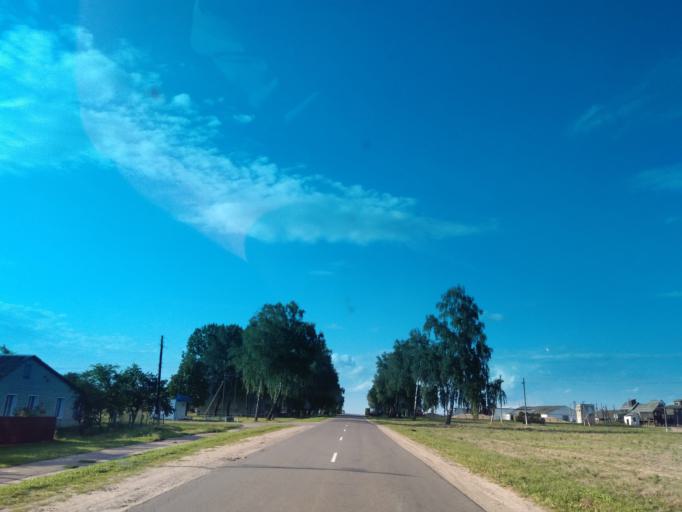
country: BY
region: Minsk
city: Kapyl'
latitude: 53.2607
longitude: 26.9576
